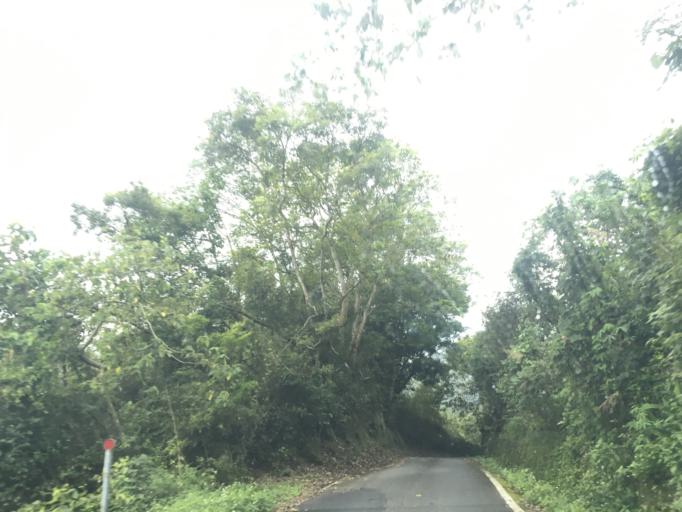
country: TW
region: Taiwan
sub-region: Yunlin
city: Douliu
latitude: 23.5673
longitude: 120.6324
